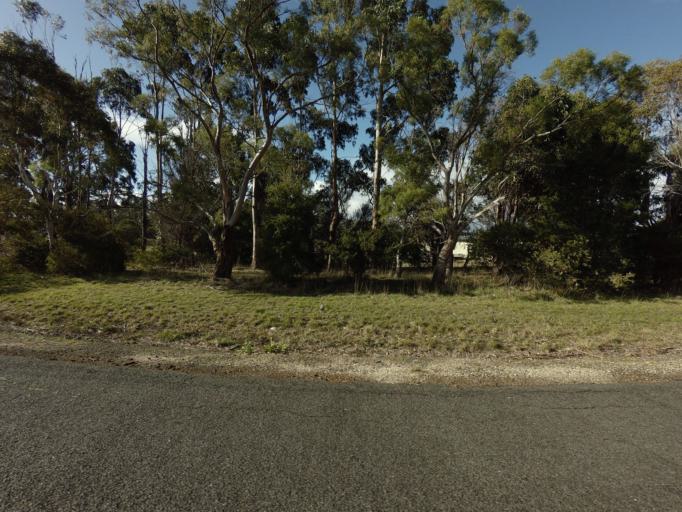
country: AU
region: Tasmania
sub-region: Sorell
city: Sorell
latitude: -42.3069
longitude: 147.9905
